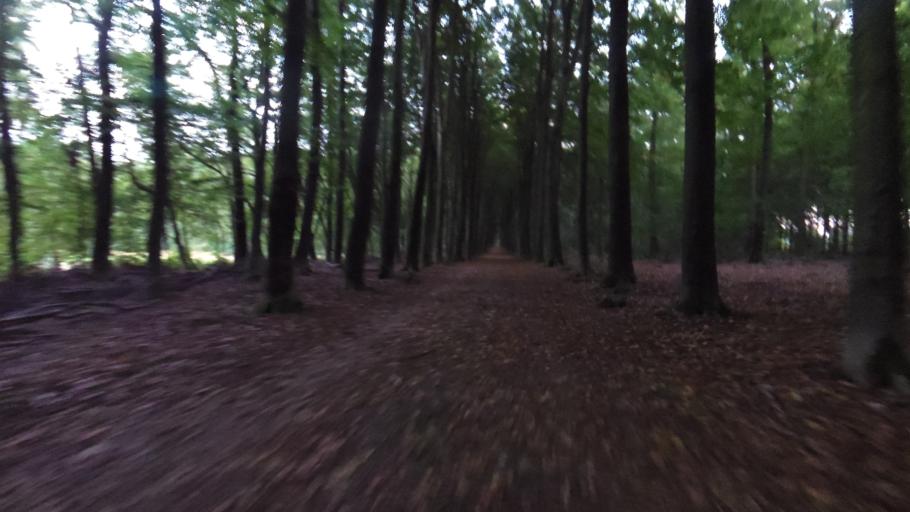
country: NL
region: Gelderland
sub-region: Gemeente Renkum
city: Doorwerth
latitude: 51.9851
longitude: 5.8125
